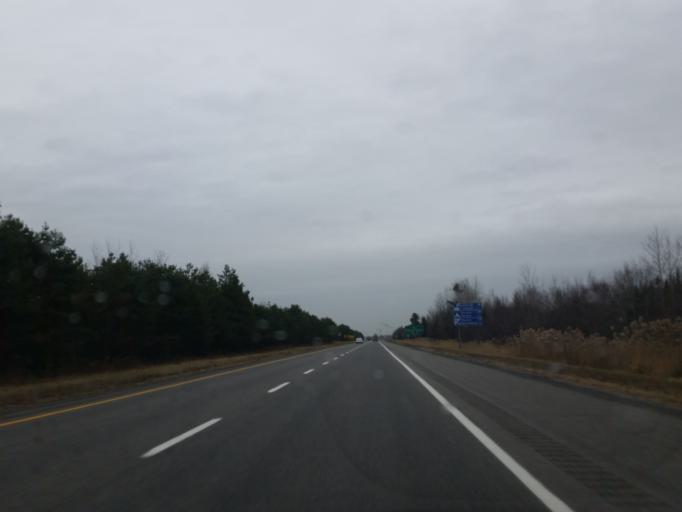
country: CA
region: Quebec
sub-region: Mauricie
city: Becancour
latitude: 46.5073
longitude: -72.2978
